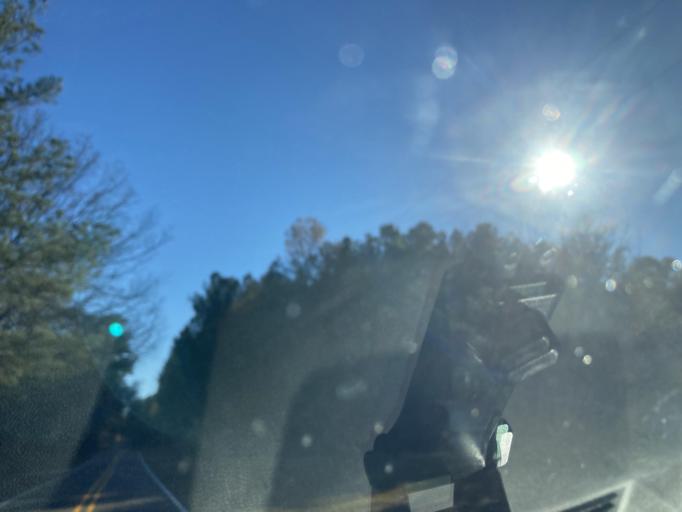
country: US
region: Mississippi
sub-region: Lamar County
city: Sumrall
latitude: 31.3616
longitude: -89.5693
